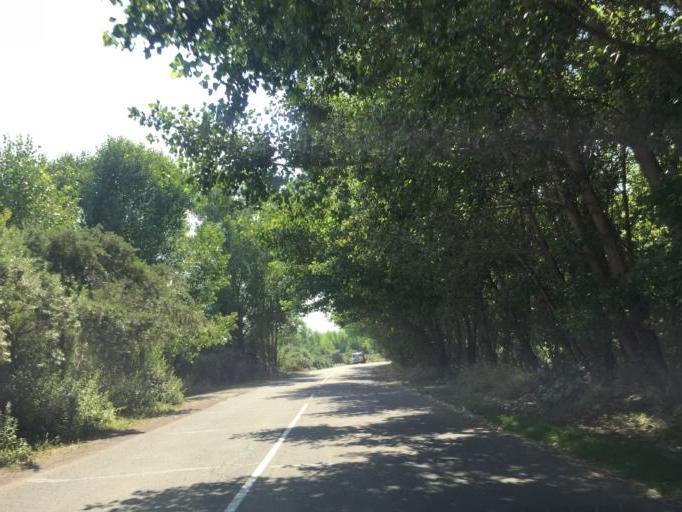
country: AM
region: Geghark'unik'i Marz
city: Artsvanist
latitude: 40.1601
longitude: 45.4984
